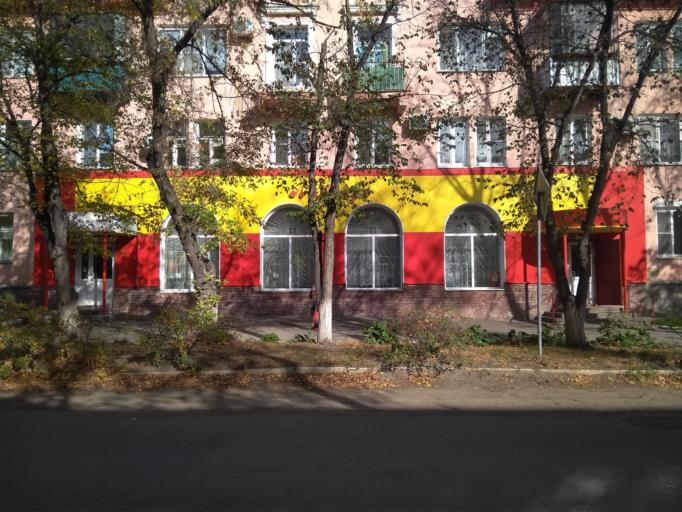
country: RU
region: Chelyabinsk
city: Troitsk
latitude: 54.0442
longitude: 61.6306
